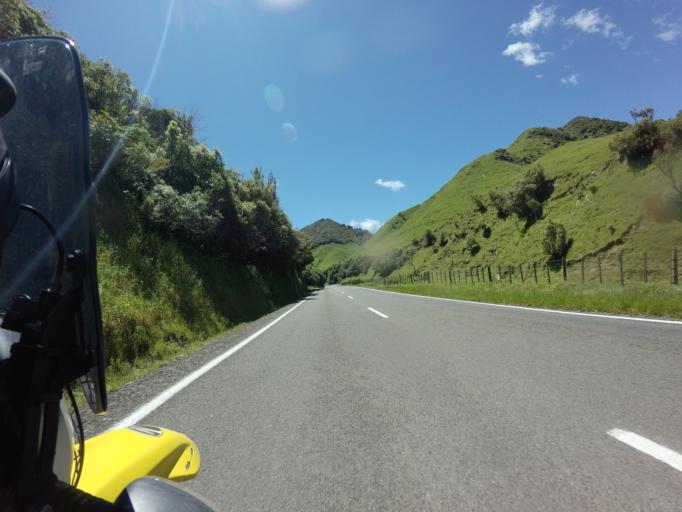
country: NZ
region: Bay of Plenty
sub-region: Opotiki District
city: Opotiki
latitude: -38.3732
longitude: 177.4645
